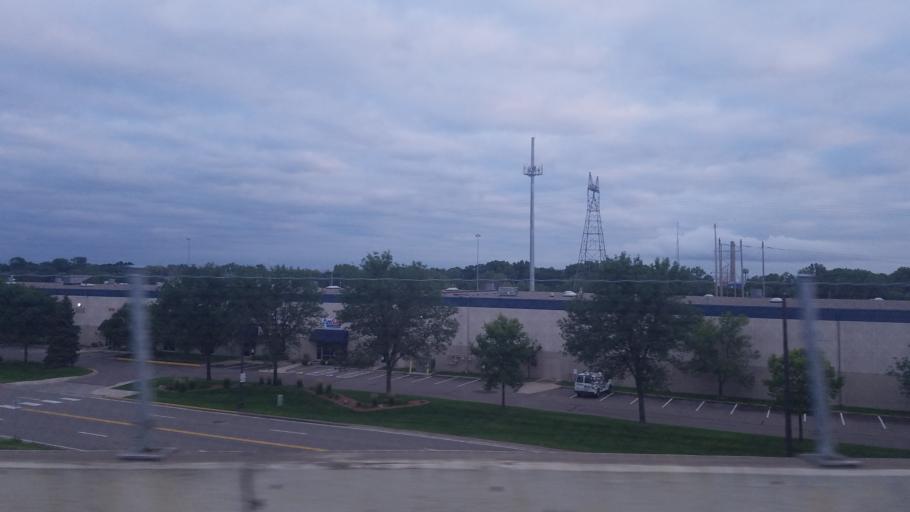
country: US
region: Minnesota
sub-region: Ramsey County
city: Falcon Heights
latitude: 44.9737
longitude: -93.1822
